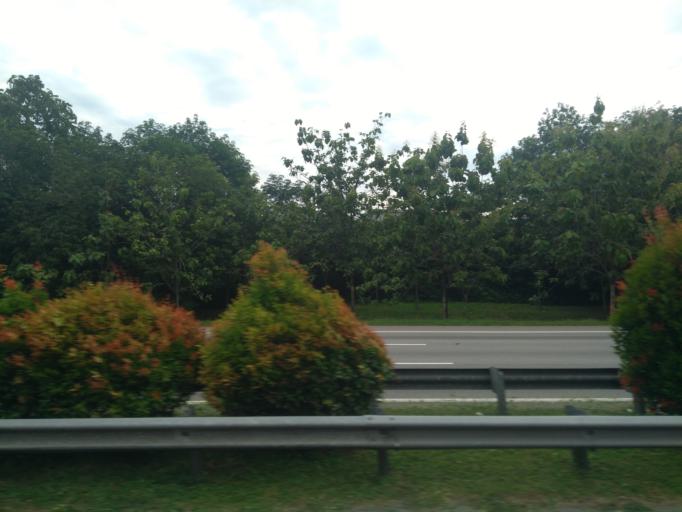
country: MY
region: Melaka
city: Pulau Sebang
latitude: 2.4290
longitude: 102.2086
